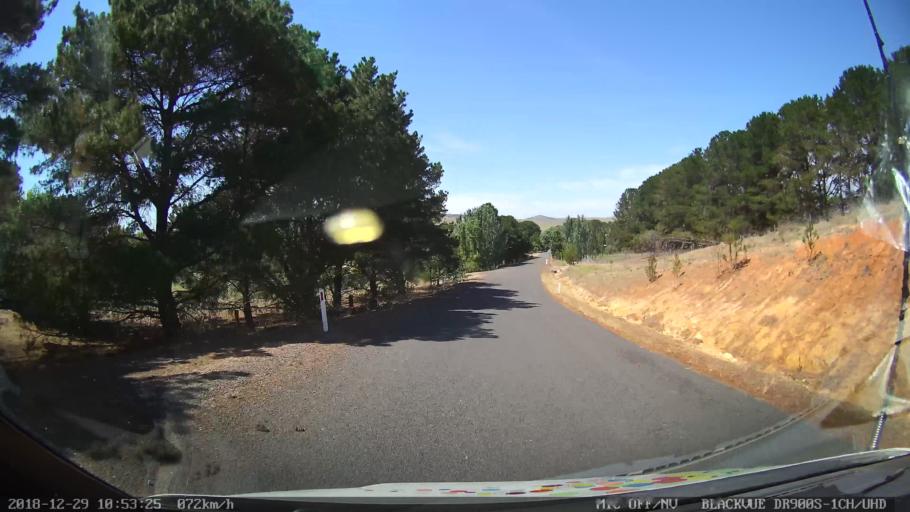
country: AU
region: New South Wales
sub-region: Palerang
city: Bungendore
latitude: -35.1083
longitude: 149.5219
